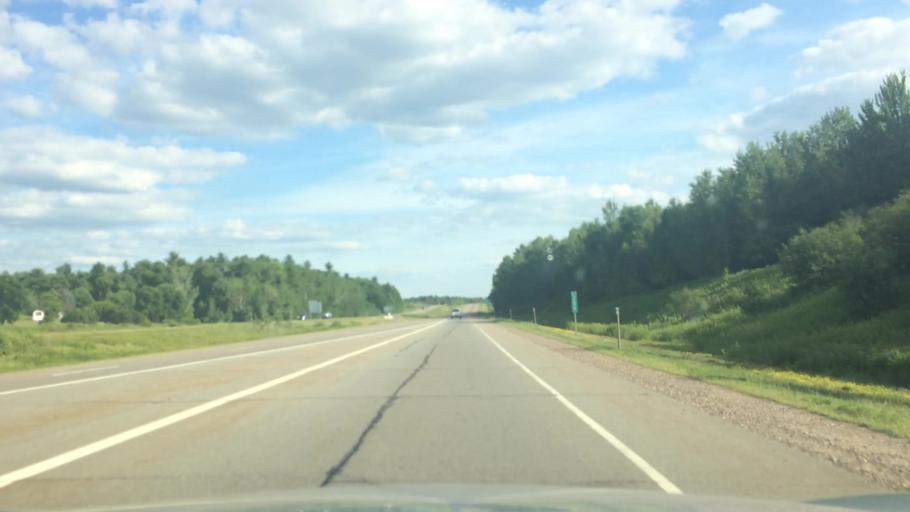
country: US
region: Wisconsin
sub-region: Lincoln County
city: Merrill
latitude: 45.1737
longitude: -89.6467
